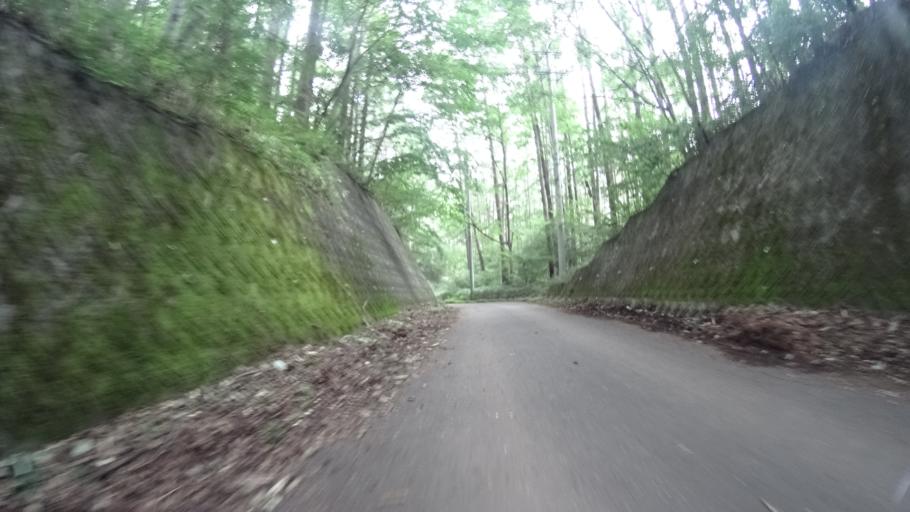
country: JP
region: Yamanashi
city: Nirasaki
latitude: 35.8974
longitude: 138.4195
